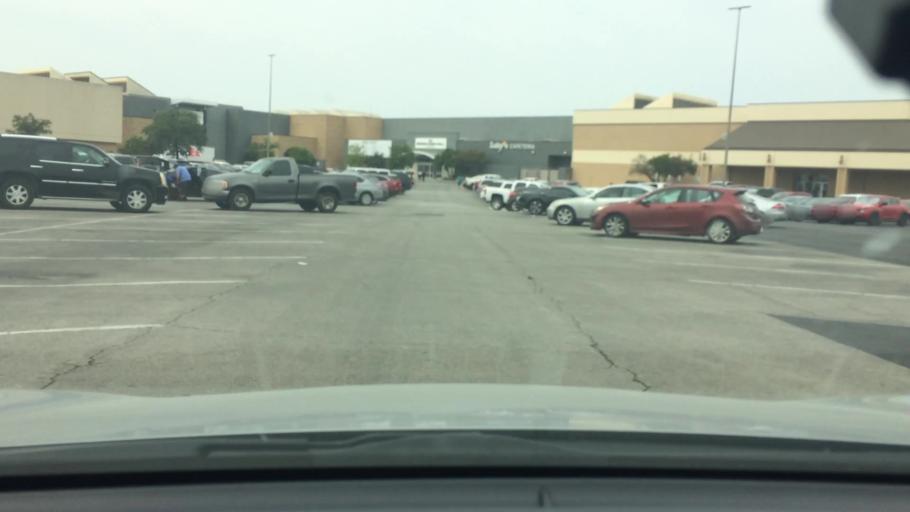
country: US
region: Texas
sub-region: Bexar County
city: Leon Valley
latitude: 29.4670
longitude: -98.6203
